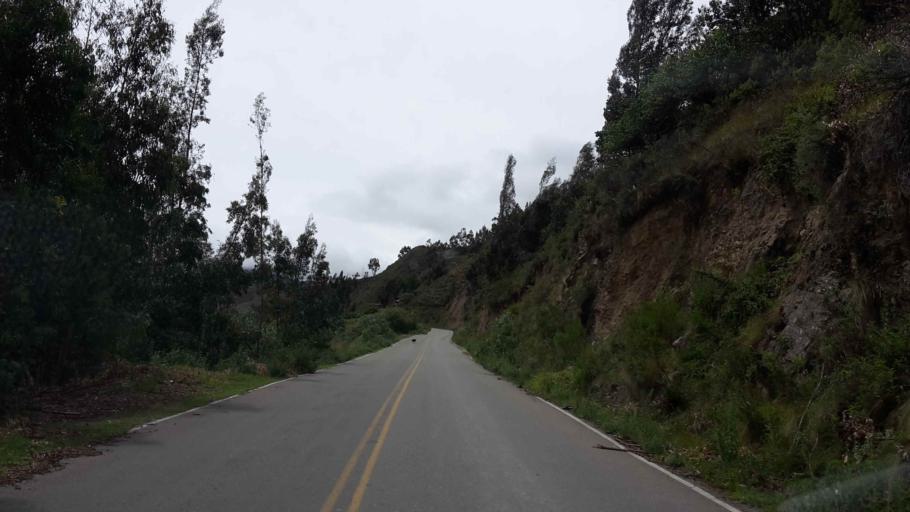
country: BO
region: Cochabamba
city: Colomi
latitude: -17.4036
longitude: -65.7912
